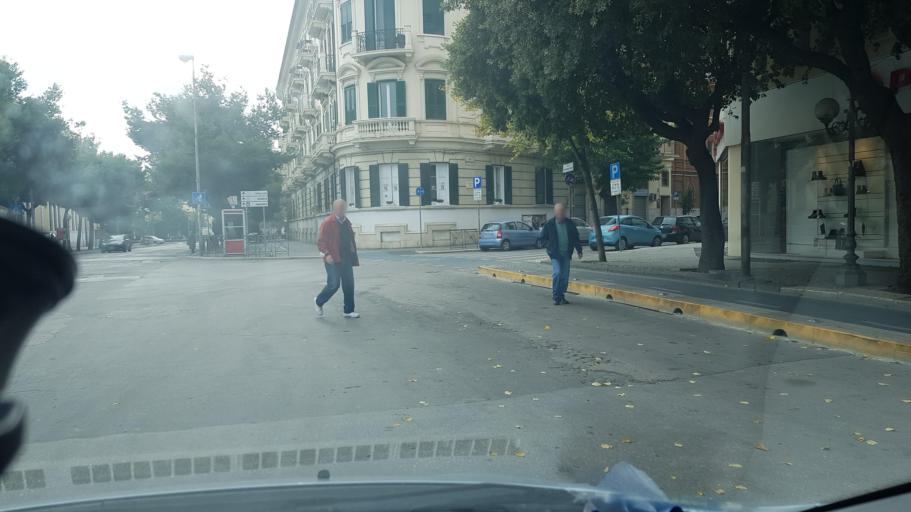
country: IT
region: Apulia
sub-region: Provincia di Foggia
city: Foggia
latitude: 41.4615
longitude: 15.5529
